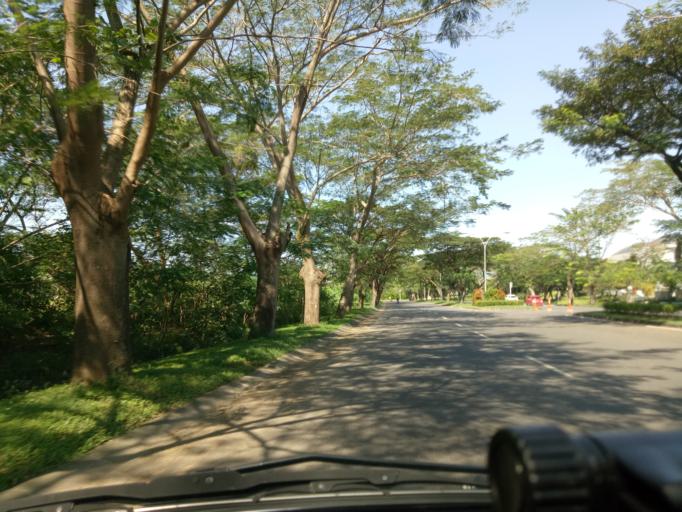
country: ID
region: East Java
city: Driyorejo
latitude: -7.2822
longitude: 112.6434
